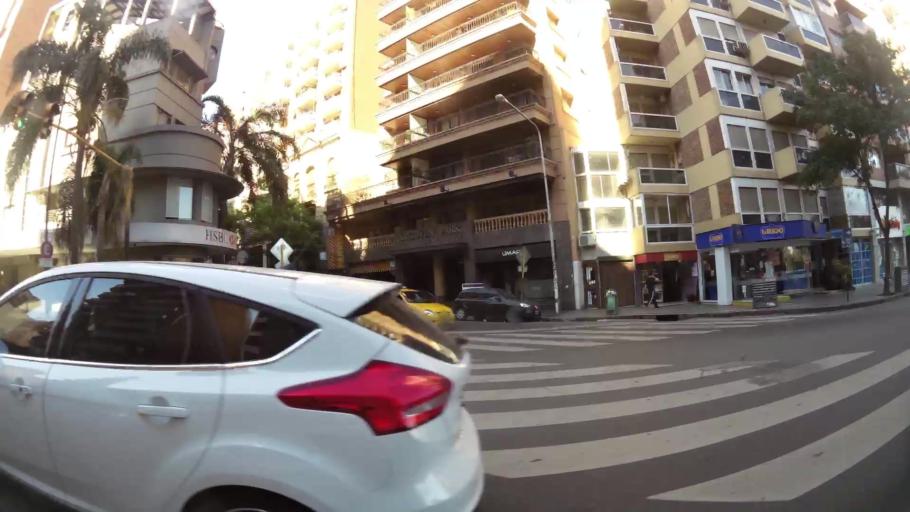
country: AR
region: Cordoba
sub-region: Departamento de Capital
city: Cordoba
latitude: -31.4253
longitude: -64.1865
